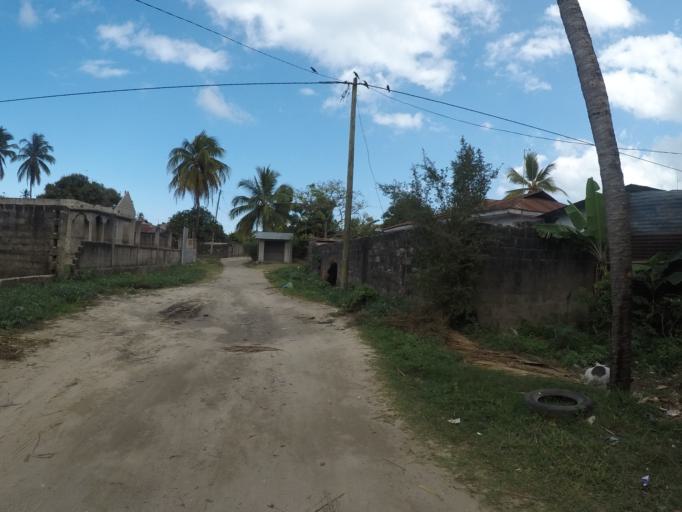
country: TZ
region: Zanzibar Urban/West
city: Zanzibar
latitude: -6.1866
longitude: 39.2146
